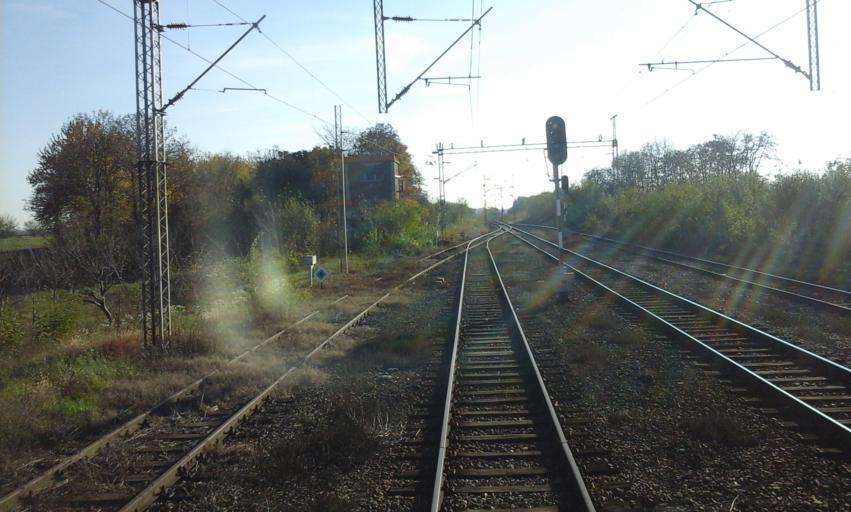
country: RS
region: Autonomna Pokrajina Vojvodina
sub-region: Severnobacki Okrug
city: Mali Igos
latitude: 45.6717
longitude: 19.6488
